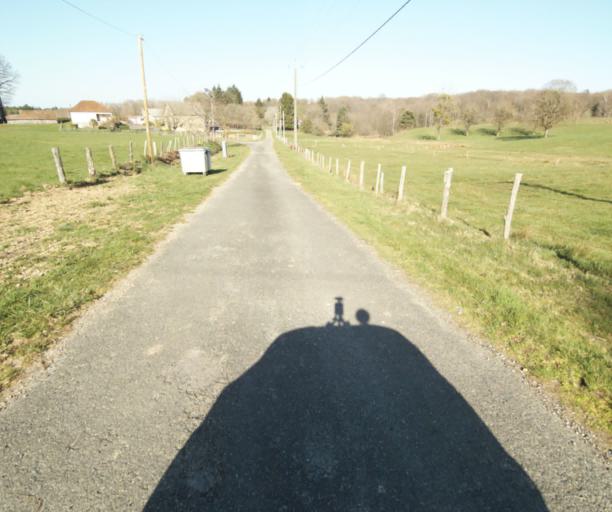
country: FR
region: Limousin
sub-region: Departement de la Correze
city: Saint-Clement
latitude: 45.3129
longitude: 1.6826
